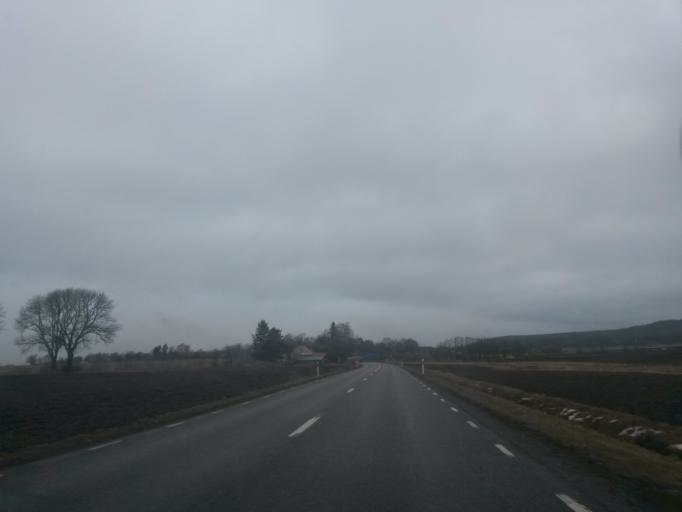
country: SE
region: Vaestra Goetaland
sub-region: Vanersborgs Kommun
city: Vargon
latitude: 58.2852
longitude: 12.3954
